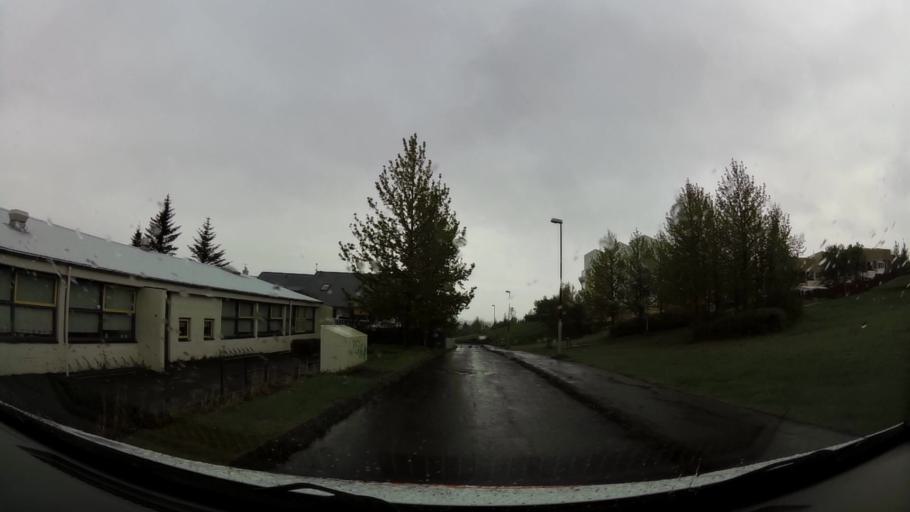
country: IS
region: Capital Region
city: Reykjavik
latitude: 64.0984
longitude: -21.8390
